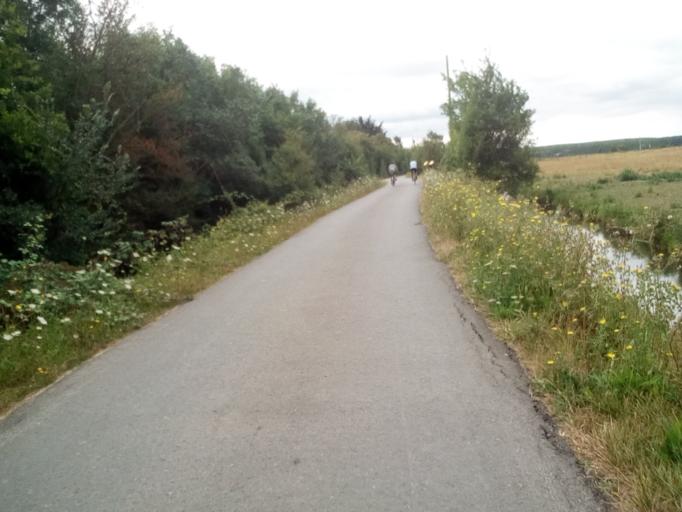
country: FR
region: Lower Normandy
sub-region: Departement du Calvados
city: Cabourg
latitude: 49.2591
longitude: -0.1325
